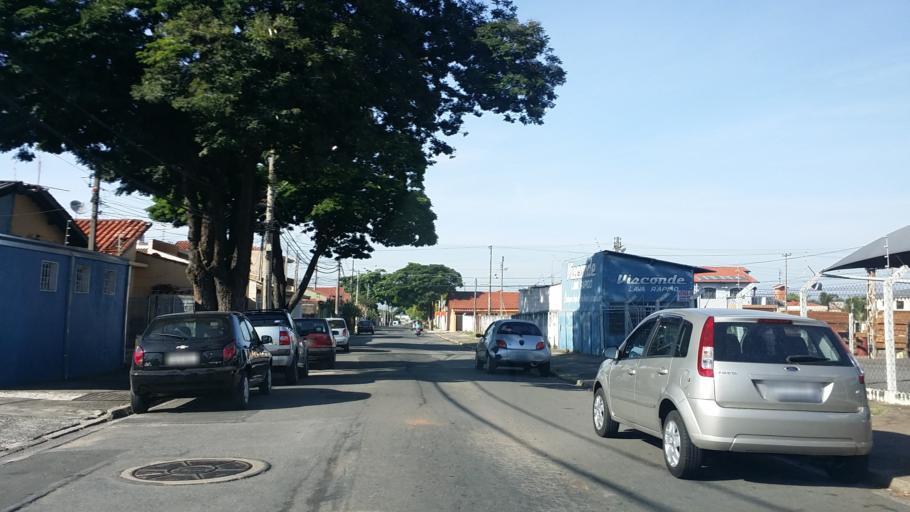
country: BR
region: Sao Paulo
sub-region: Indaiatuba
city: Indaiatuba
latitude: -23.0917
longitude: -47.1963
